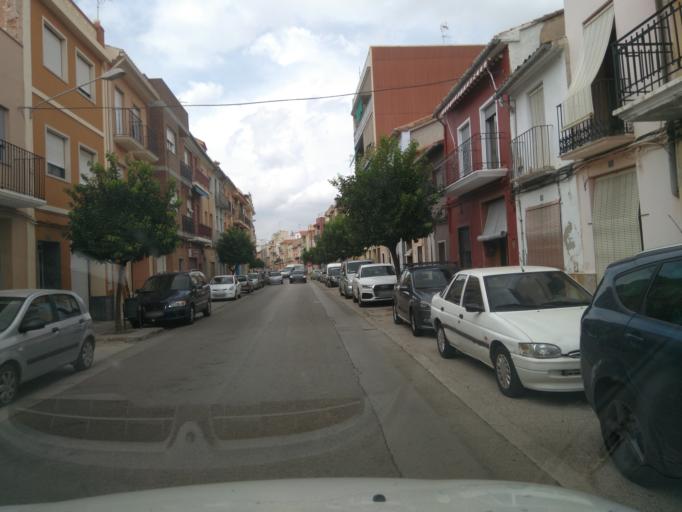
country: ES
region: Valencia
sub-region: Provincia de Valencia
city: Carcaixent
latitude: 39.1187
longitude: -0.4436
